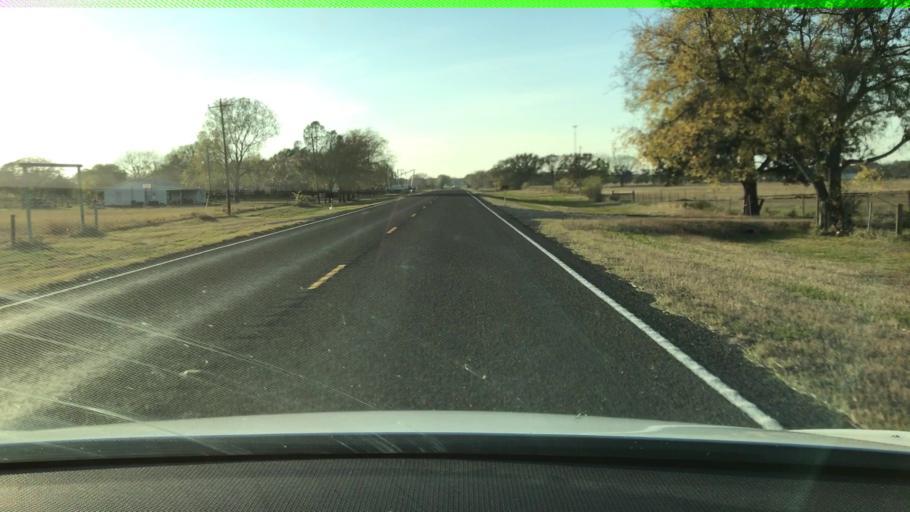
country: US
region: Texas
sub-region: Kaufman County
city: Kemp
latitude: 32.5700
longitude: -96.1137
